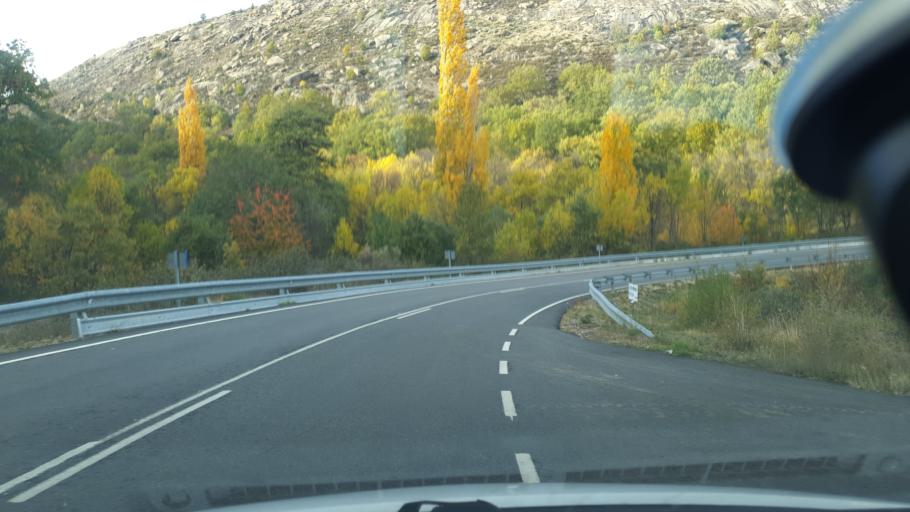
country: ES
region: Castille and Leon
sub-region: Provincia de Avila
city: Navalosa
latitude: 40.3978
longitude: -4.9109
